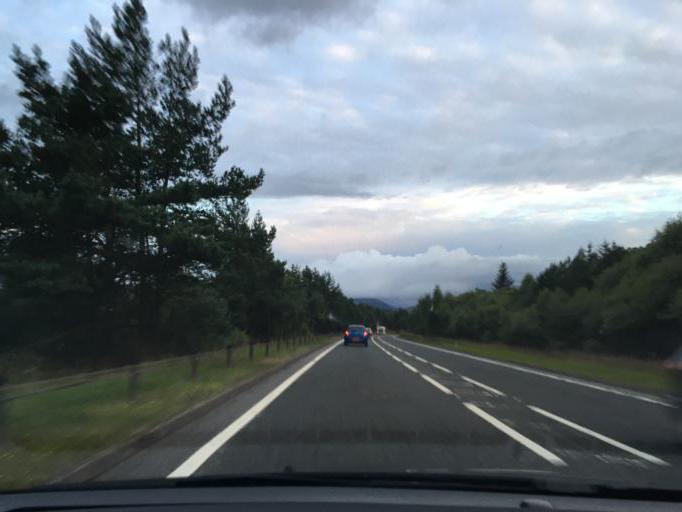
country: GB
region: Scotland
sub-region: Highland
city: Aviemore
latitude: 57.1814
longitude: -3.8351
